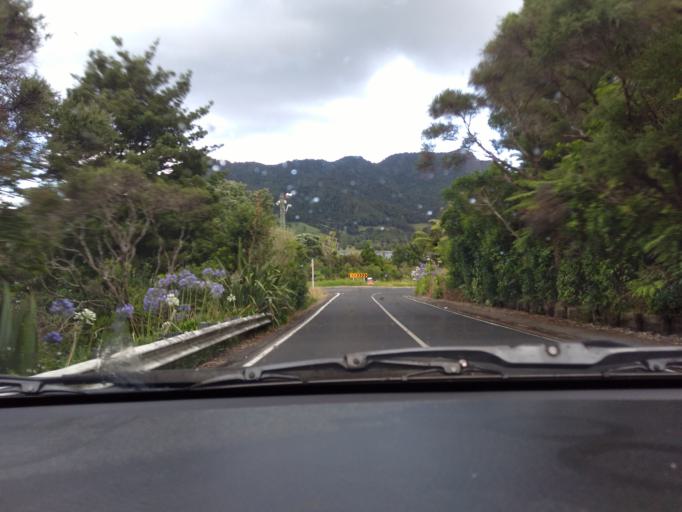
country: NZ
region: Auckland
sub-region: Auckland
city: Titirangi
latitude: -37.0035
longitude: 174.5732
